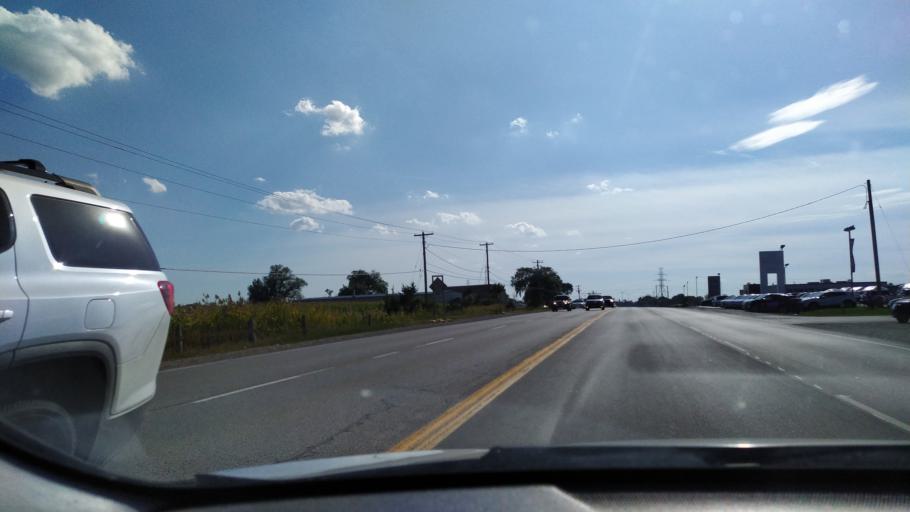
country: CA
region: Ontario
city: London
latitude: 42.9259
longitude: -81.2747
